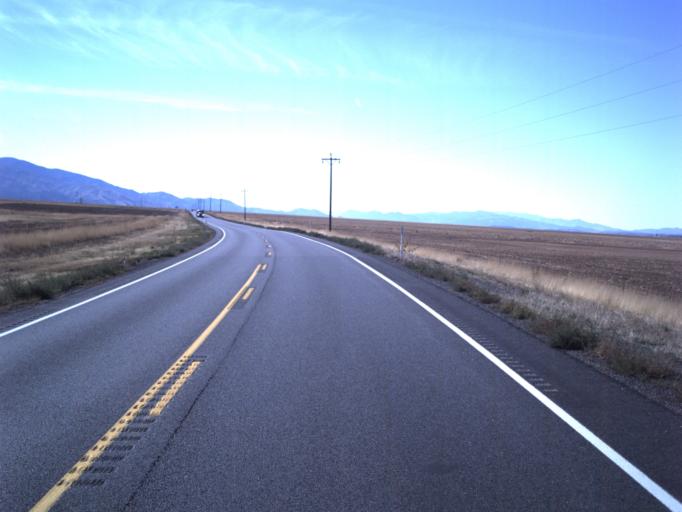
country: US
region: Utah
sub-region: Juab County
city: Nephi
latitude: 39.6449
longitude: -111.8613
